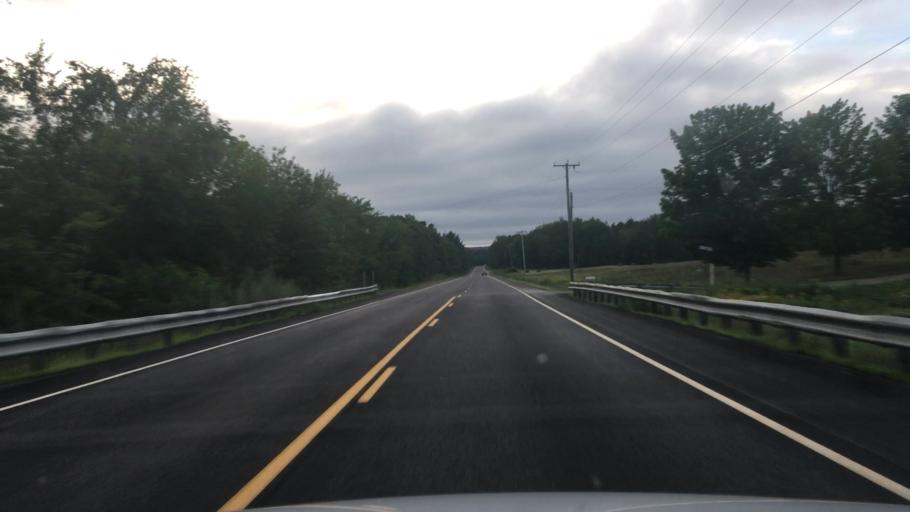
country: US
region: Maine
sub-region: Waldo County
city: Searsmont
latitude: 44.4023
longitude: -69.1643
